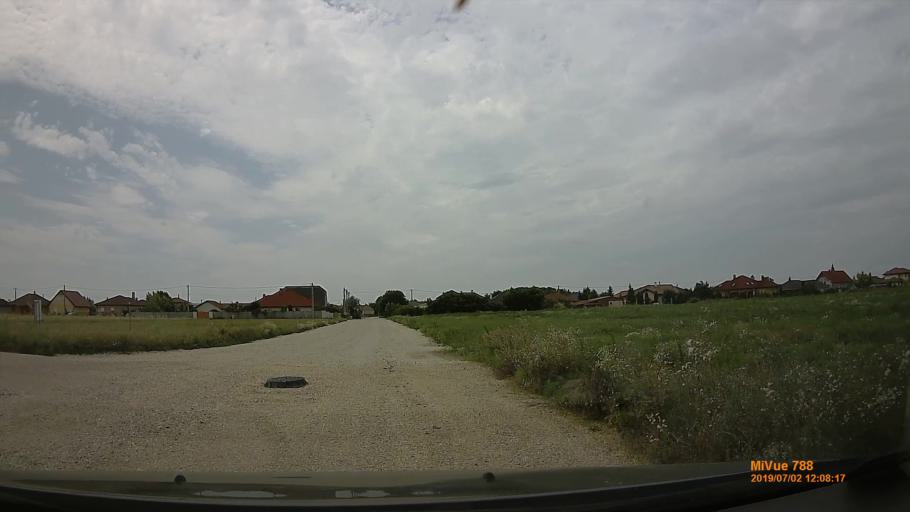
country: HU
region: Gyor-Moson-Sopron
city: Janossomorja
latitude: 47.8534
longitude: 17.1840
